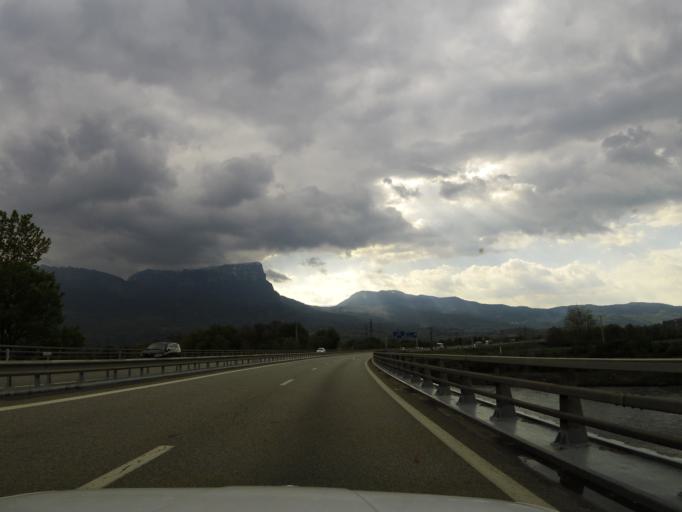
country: FR
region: Rhone-Alpes
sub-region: Departement de la Savoie
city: Montmelian
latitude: 45.4818
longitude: 6.0339
